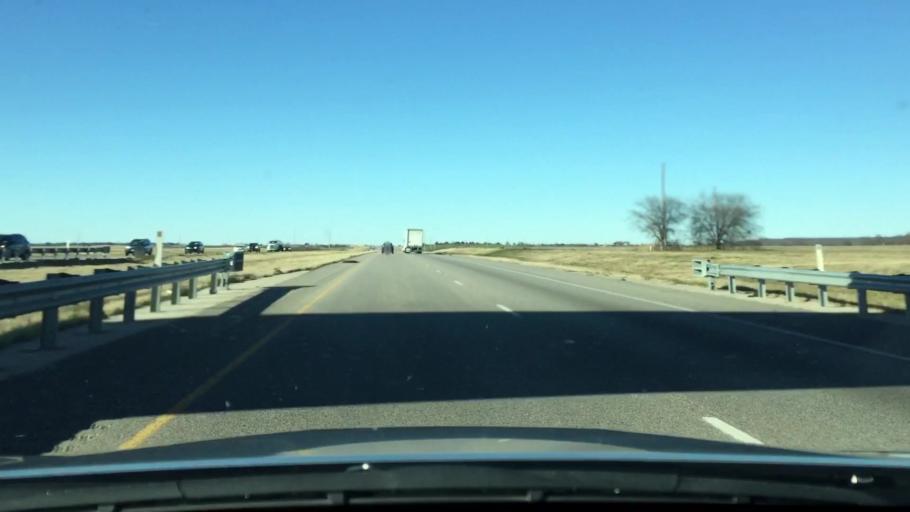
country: US
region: Texas
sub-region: Hill County
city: Itasca
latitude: 32.1264
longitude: -97.1179
